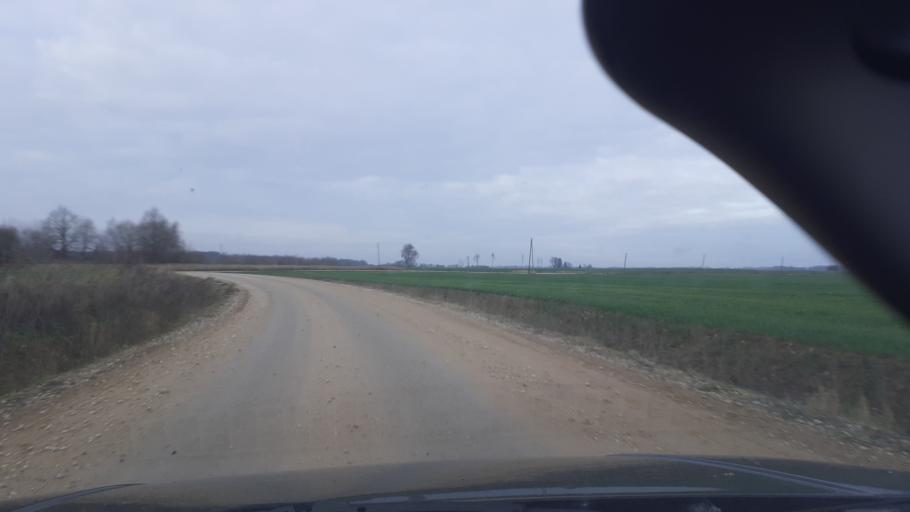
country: LV
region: Aizpute
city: Aizpute
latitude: 56.8553
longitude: 21.6675
